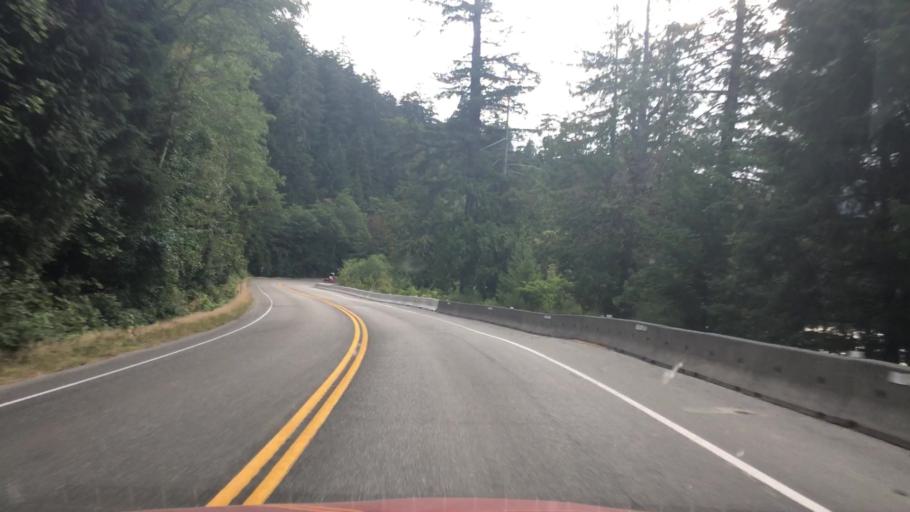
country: CA
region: British Columbia
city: Port Alberni
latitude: 49.2885
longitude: -124.6135
